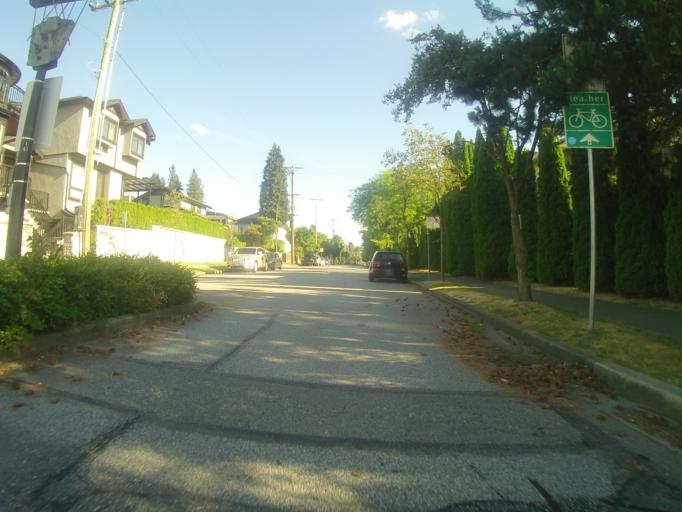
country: CA
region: British Columbia
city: Vancouver
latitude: 49.2489
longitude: -123.1204
